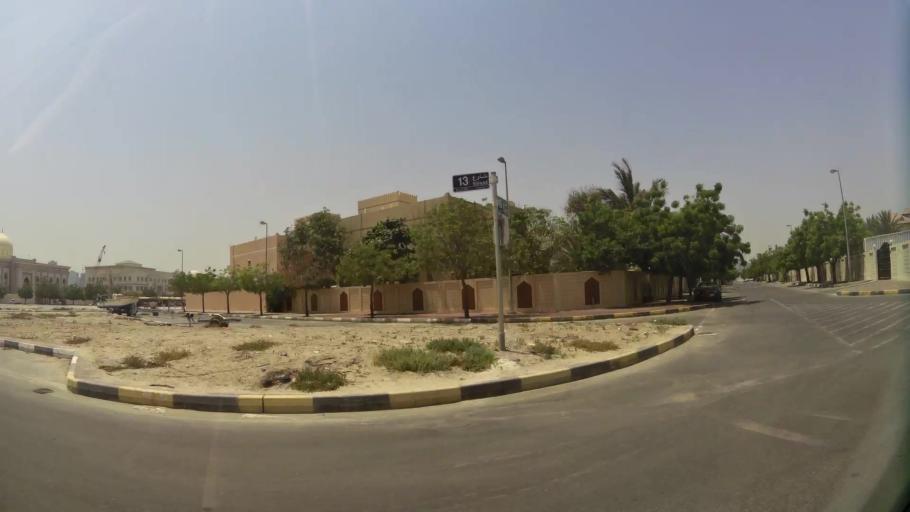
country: AE
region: Ash Shariqah
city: Sharjah
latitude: 25.3459
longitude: 55.3738
